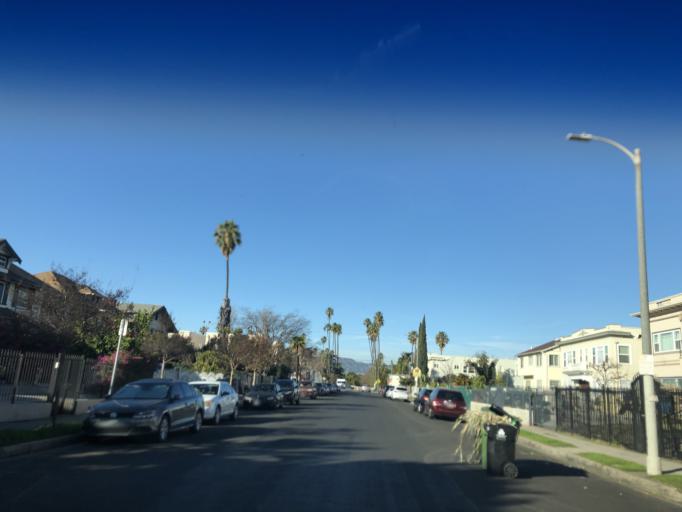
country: US
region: California
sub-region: Los Angeles County
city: Hollywood
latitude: 34.0458
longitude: -118.3157
